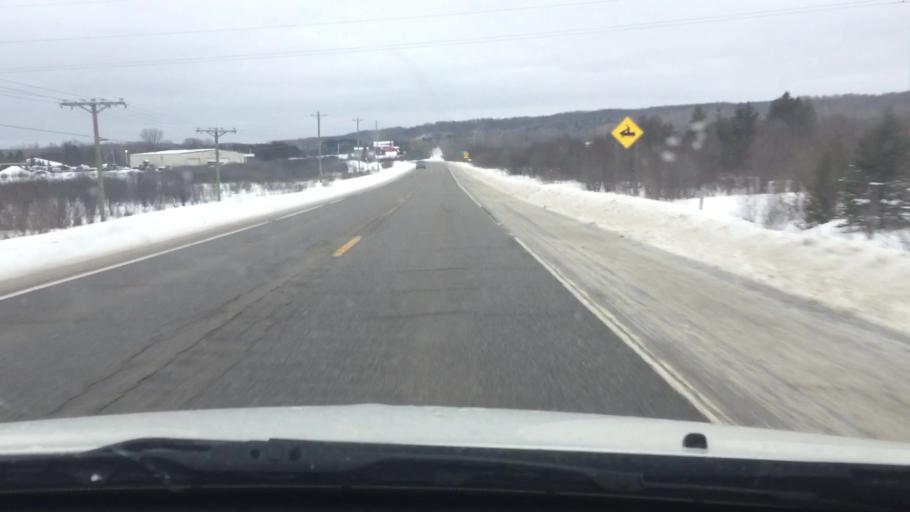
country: US
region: Michigan
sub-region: Charlevoix County
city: East Jordan
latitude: 45.1365
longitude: -85.1398
